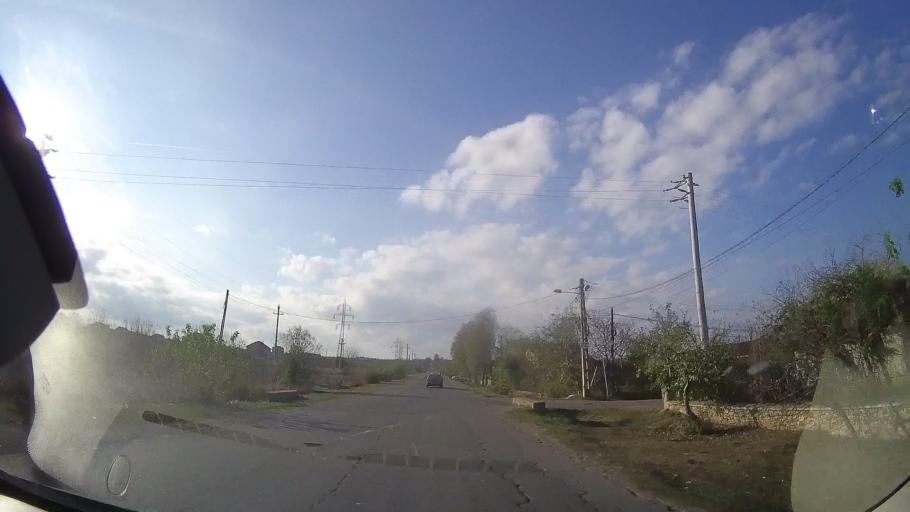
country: RO
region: Constanta
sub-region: Comuna Limanu
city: Limanu
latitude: 43.7937
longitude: 28.5402
